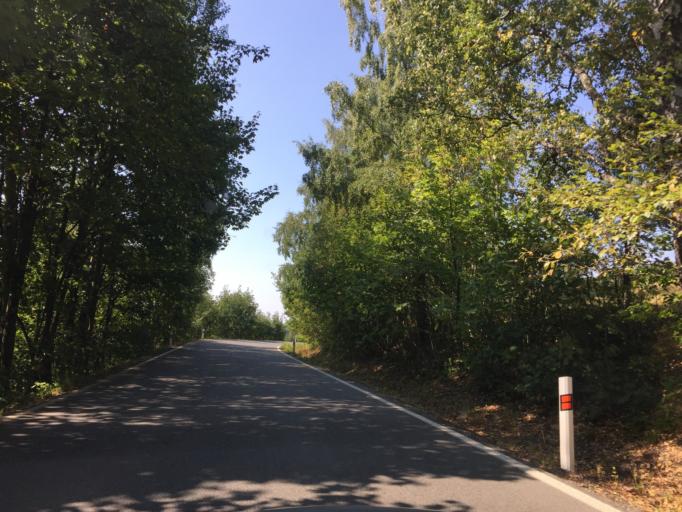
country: CZ
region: Liberecky
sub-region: Okres Jablonec nad Nisou
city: Janov nad Nisou
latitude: 50.7847
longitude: 15.1737
